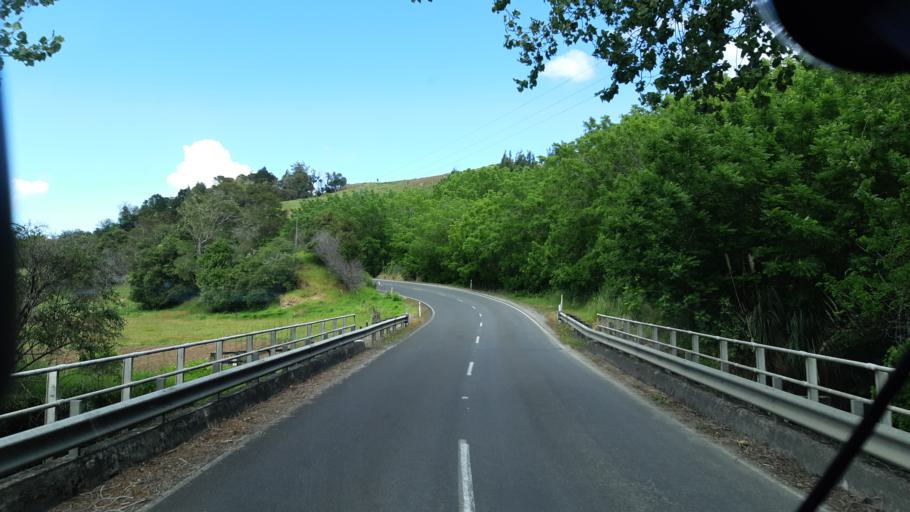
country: NZ
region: Northland
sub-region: Far North District
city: Taipa
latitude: -35.2612
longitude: 173.5270
